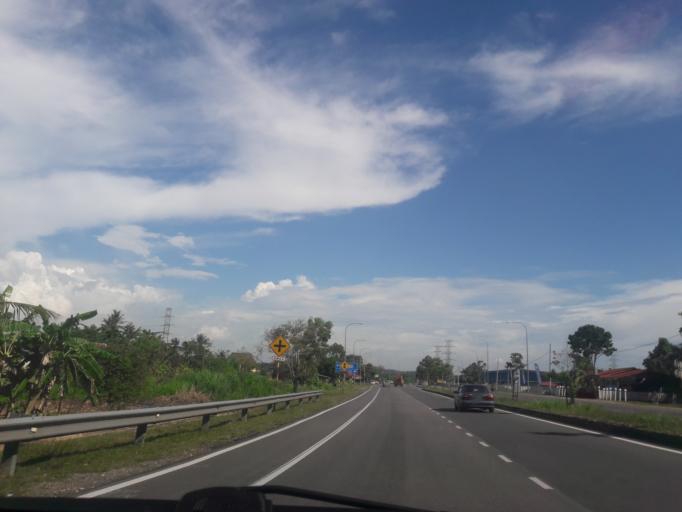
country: MY
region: Kedah
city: Sungai Petani
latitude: 5.6194
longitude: 100.4656
